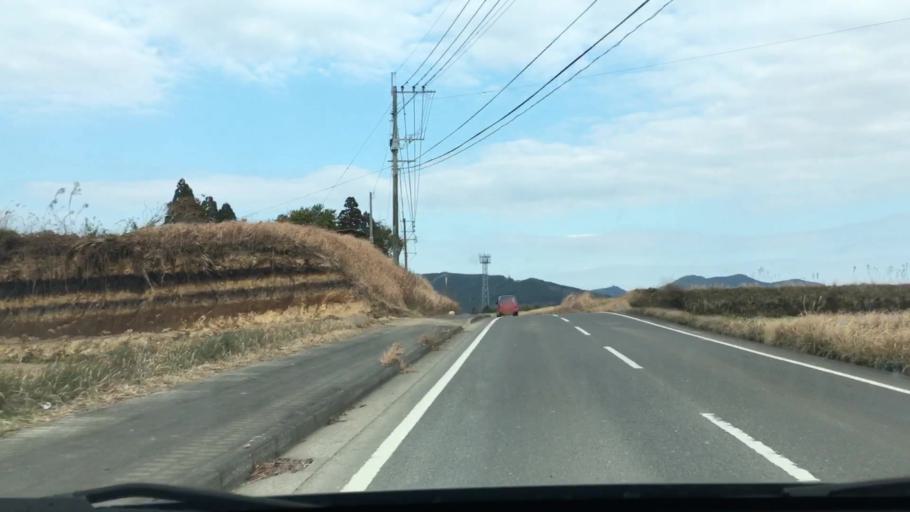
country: JP
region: Miyazaki
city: Kushima
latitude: 31.5051
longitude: 131.2413
